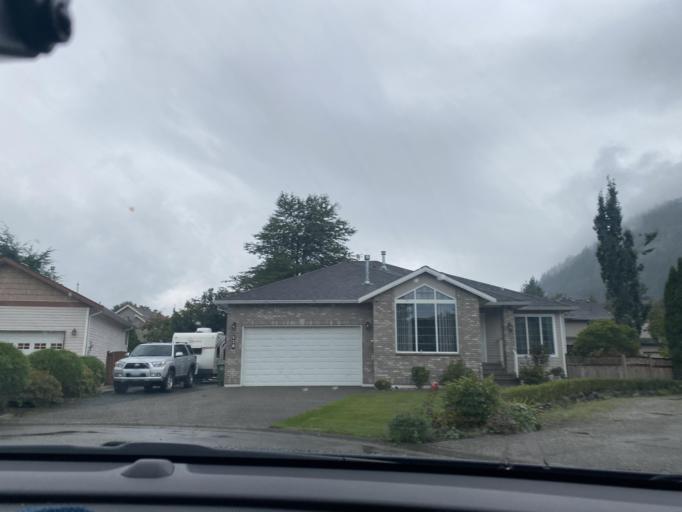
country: CA
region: British Columbia
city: Agassiz
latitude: 49.2963
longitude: -121.7792
